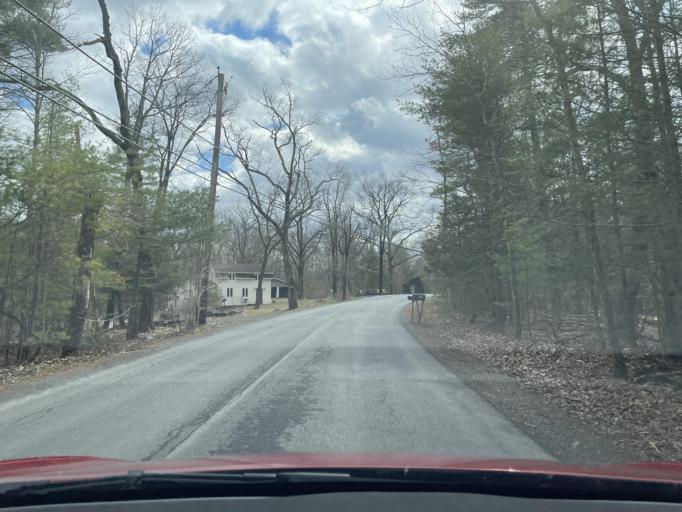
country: US
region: New York
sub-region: Ulster County
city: Zena
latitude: 42.0348
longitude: -74.0373
